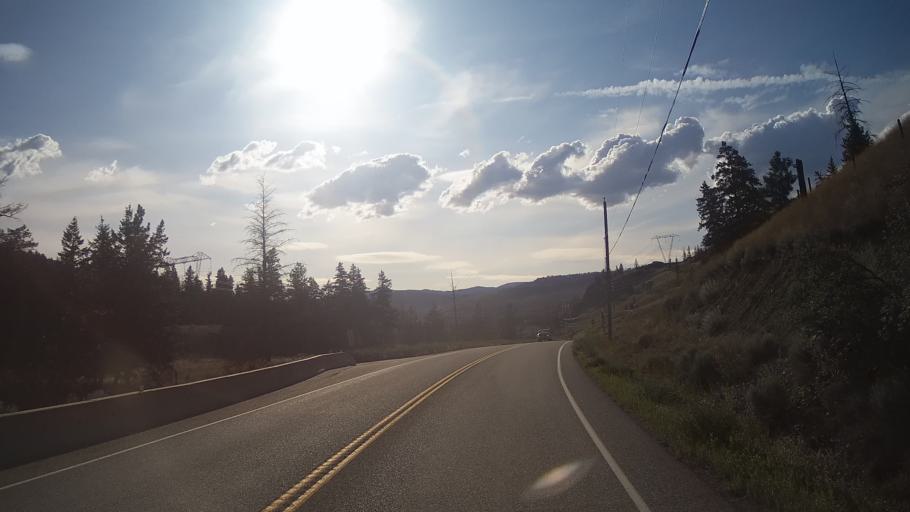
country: CA
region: British Columbia
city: Cache Creek
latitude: 50.8842
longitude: -121.4273
